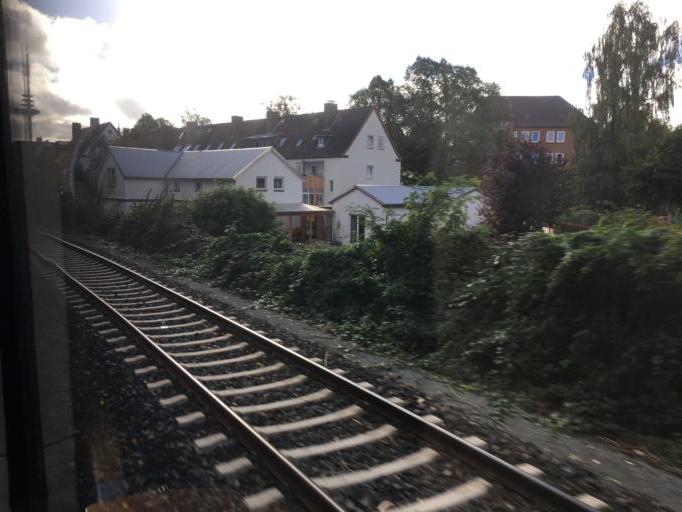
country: DE
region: Schleswig-Holstein
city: Kronshagen
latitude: 54.3066
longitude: 10.1030
